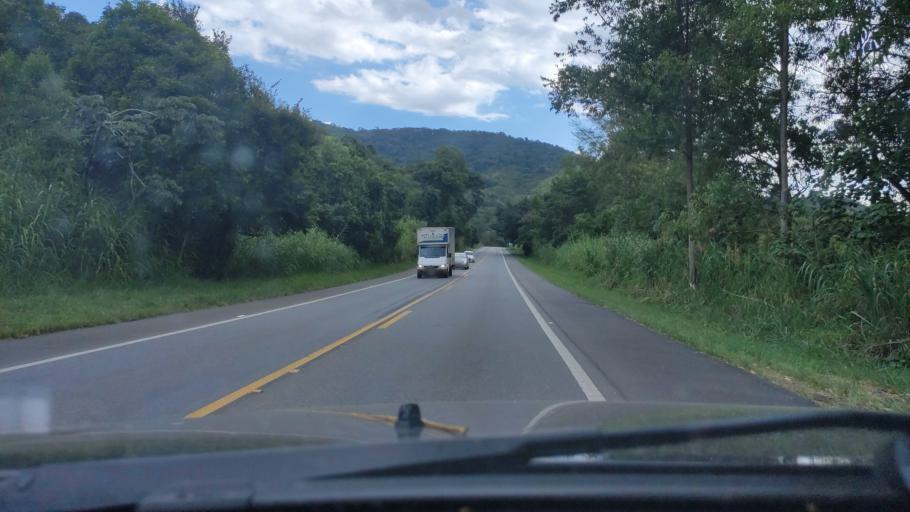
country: BR
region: Sao Paulo
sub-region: Aguas De Lindoia
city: Aguas de Lindoia
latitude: -22.4692
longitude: -46.7056
